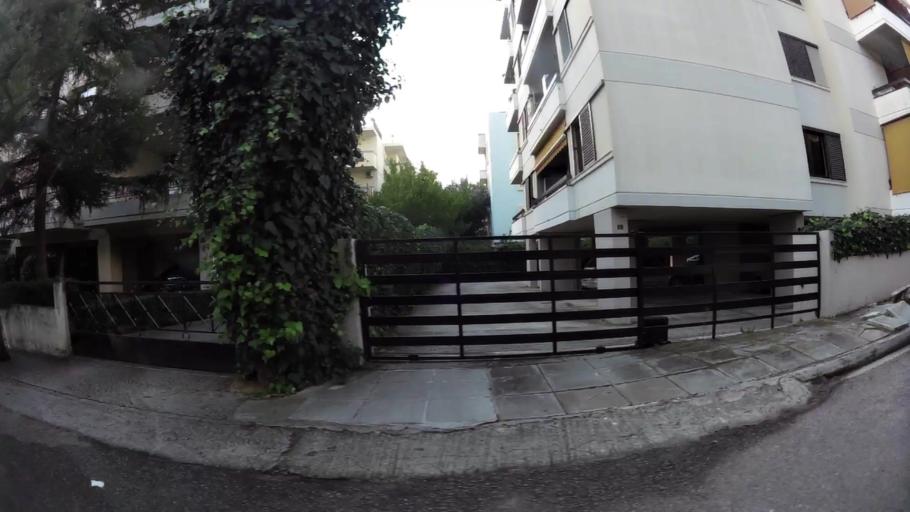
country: GR
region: Attica
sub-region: Nomarchia Athinas
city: Melissia
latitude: 38.0514
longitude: 23.8223
